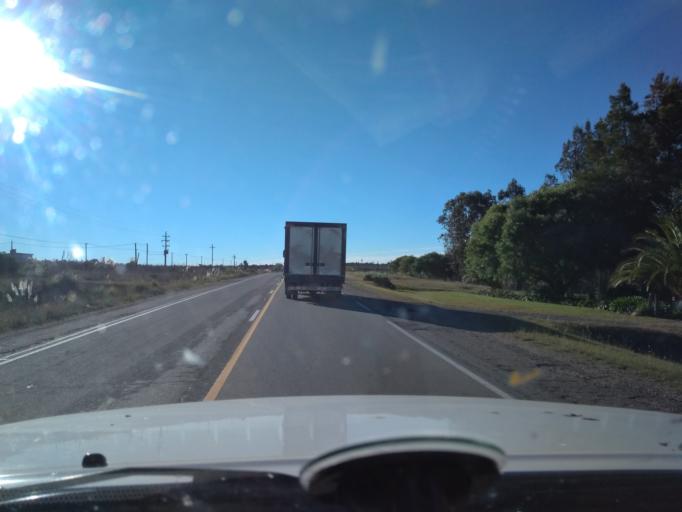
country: UY
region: Canelones
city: Sauce
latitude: -34.5900
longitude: -56.0533
